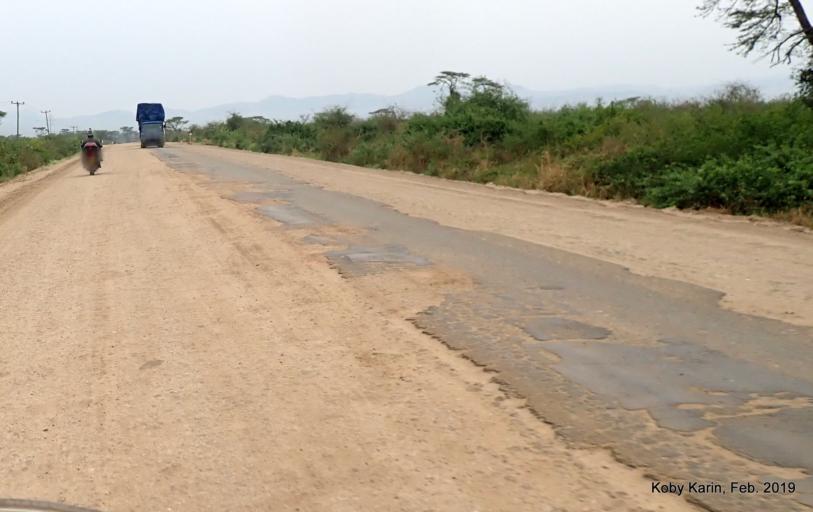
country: UG
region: Western Region
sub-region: Rubirizi District
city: Rubirizi
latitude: -0.1488
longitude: 30.0666
